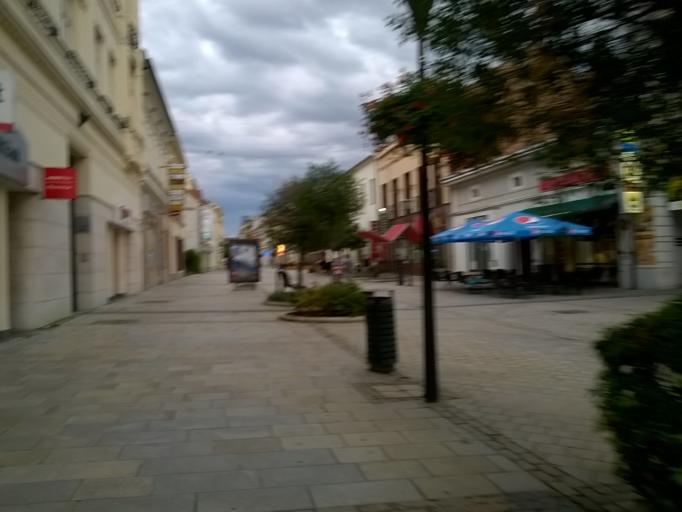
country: SK
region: Nitriansky
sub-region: Okres Nitra
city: Nitra
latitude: 48.3120
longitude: 18.0873
